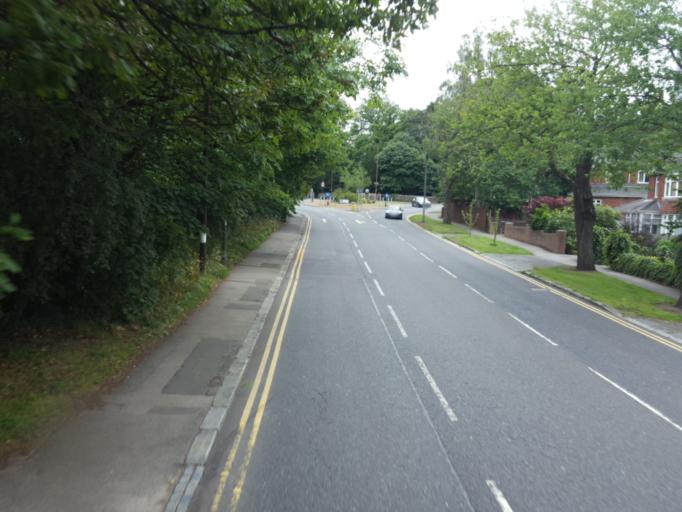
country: GB
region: England
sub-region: County Durham
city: Durham
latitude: 54.7907
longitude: -1.5906
